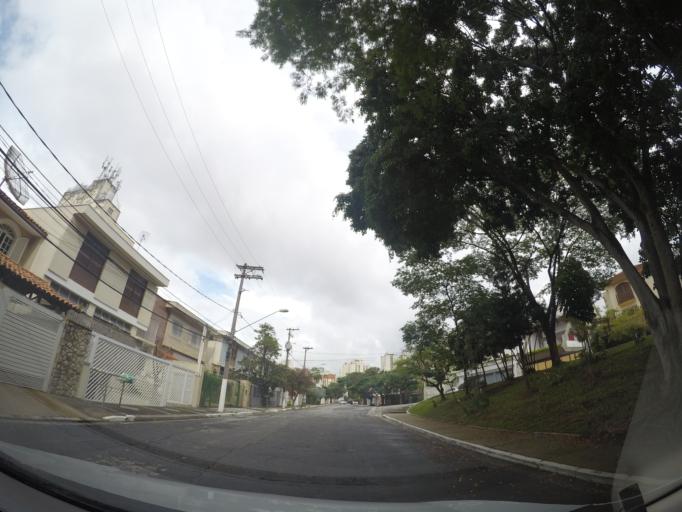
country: BR
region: Sao Paulo
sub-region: Sao Paulo
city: Sao Paulo
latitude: -23.5883
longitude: -46.6227
